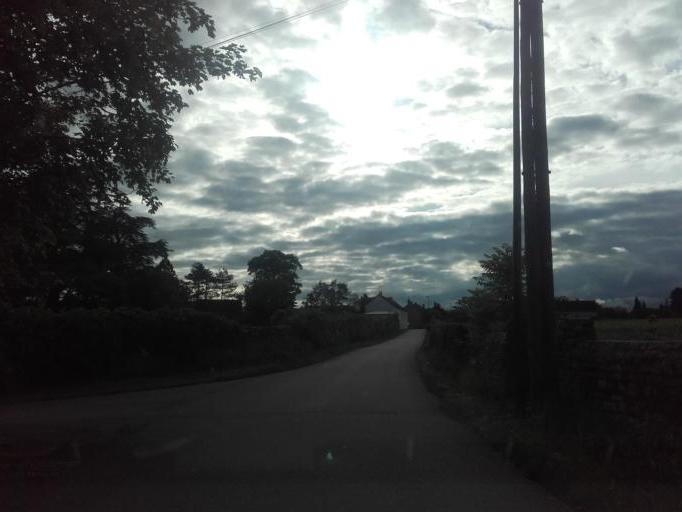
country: FR
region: Bourgogne
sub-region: Departement de Saone-et-Loire
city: Mellecey
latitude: 46.8323
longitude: 4.7368
